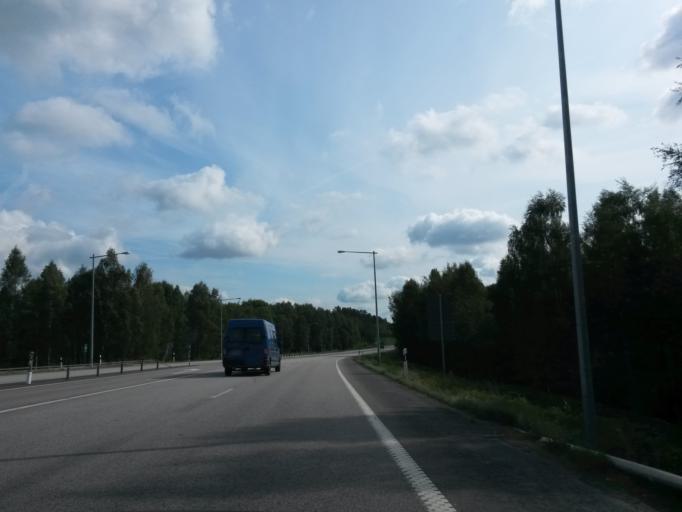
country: SE
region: Kronoberg
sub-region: Vaxjo Kommun
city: Vaexjoe
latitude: 56.8903
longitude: 14.7548
